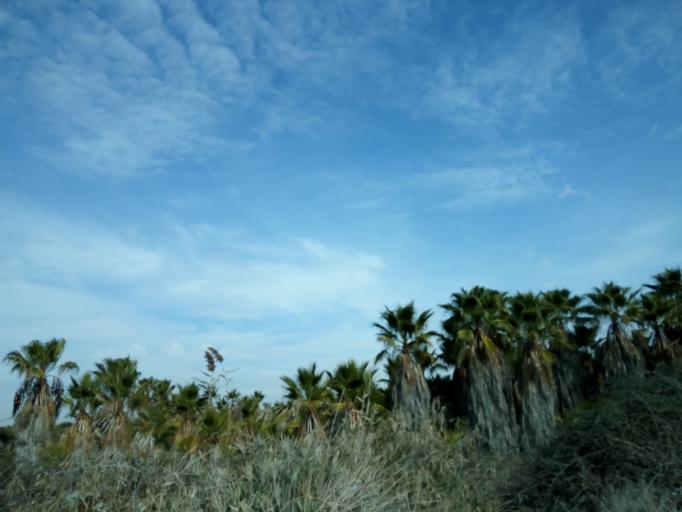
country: PT
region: Faro
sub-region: Faro
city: Faro
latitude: 37.0355
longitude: -7.9807
